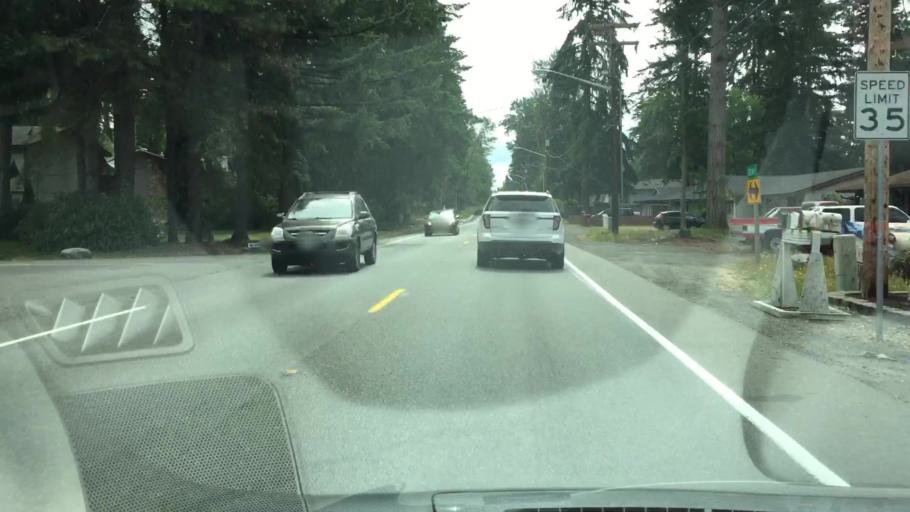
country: US
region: Washington
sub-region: Pierce County
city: South Hill
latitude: 47.1248
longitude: -122.2666
